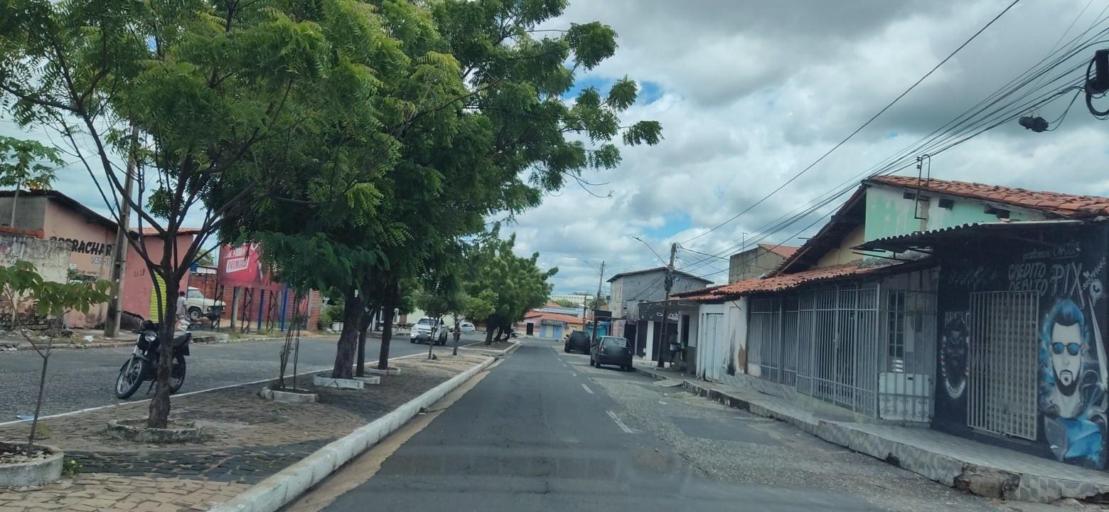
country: BR
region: Piaui
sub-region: Teresina
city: Teresina
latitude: -5.1472
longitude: -42.7801
